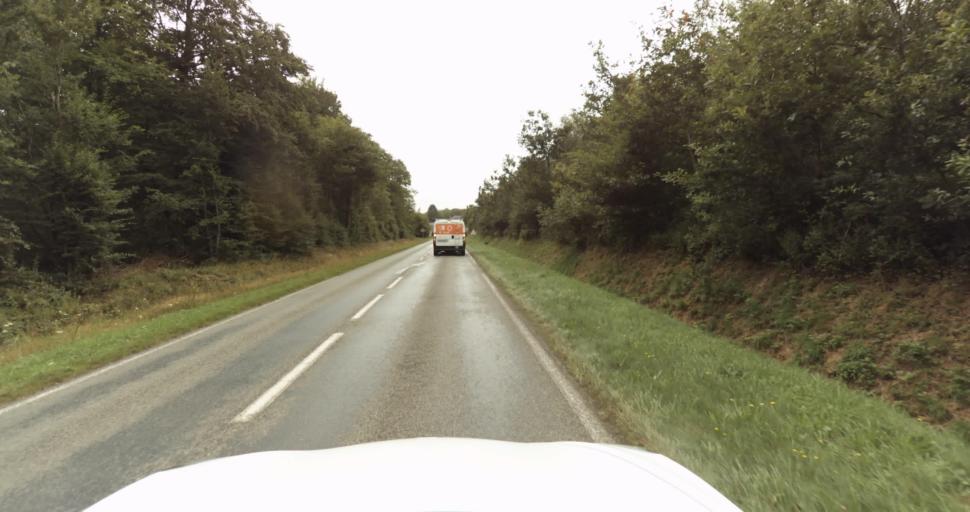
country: FR
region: Haute-Normandie
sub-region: Departement de l'Eure
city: Arnieres-sur-Iton
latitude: 48.9762
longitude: 1.0880
